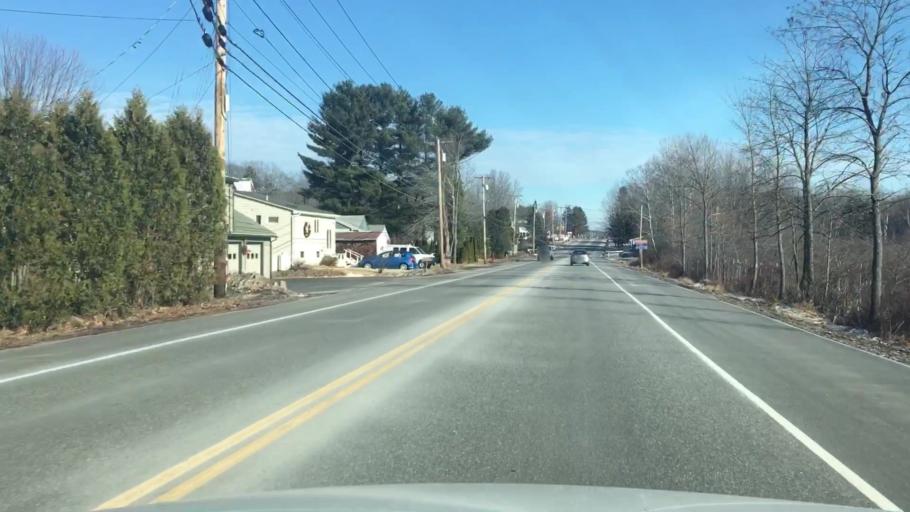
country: US
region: Maine
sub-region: Androscoggin County
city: Sabattus
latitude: 44.1191
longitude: -70.0926
